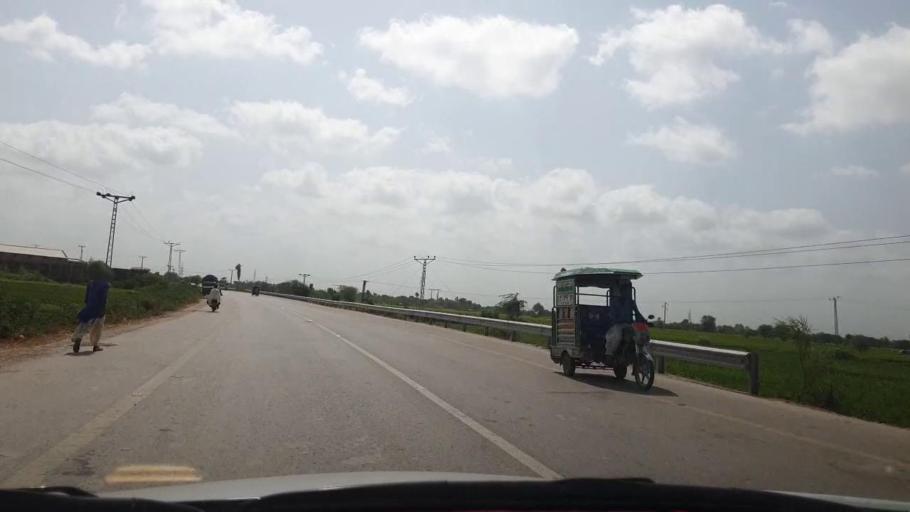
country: PK
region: Sindh
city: Talhar
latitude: 24.8894
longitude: 68.7986
